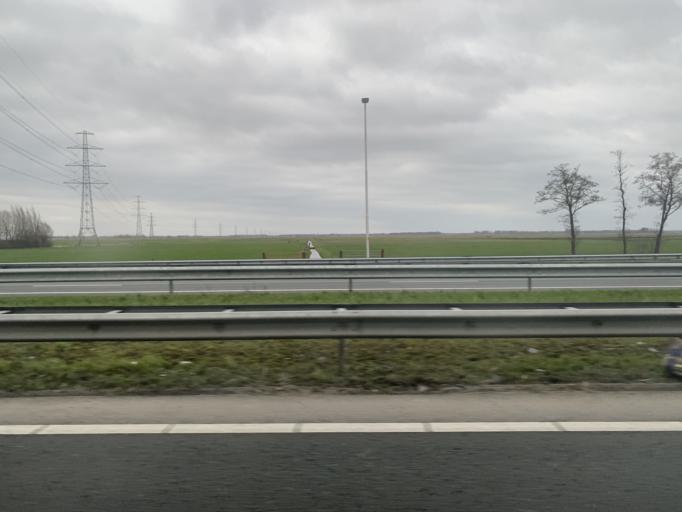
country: NL
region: Groningen
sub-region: Gemeente Zuidhorn
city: Aduard
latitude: 53.2042
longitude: 6.4814
